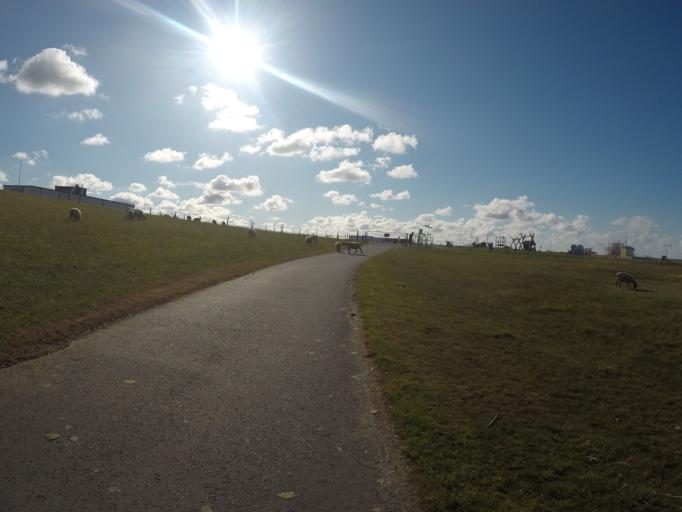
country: DE
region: Lower Saxony
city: Nordleda
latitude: 53.8339
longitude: 8.7832
